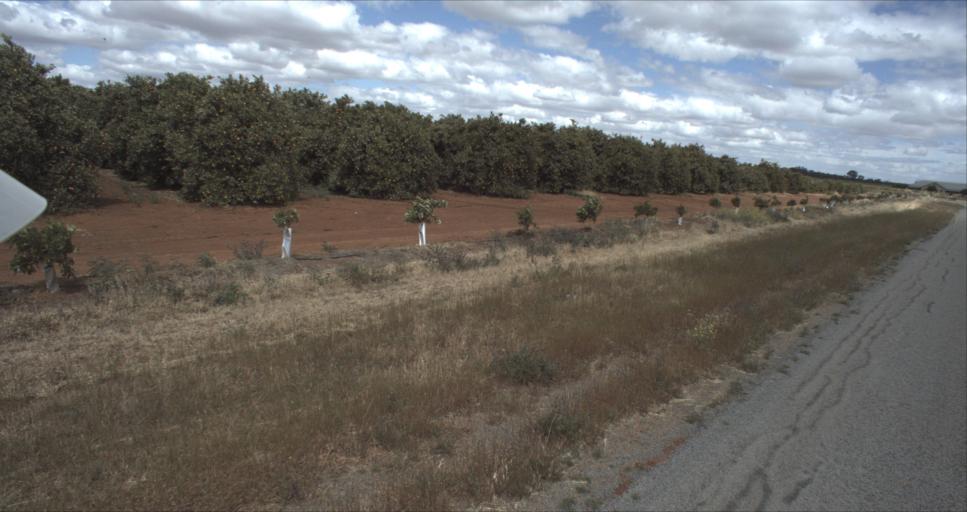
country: AU
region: New South Wales
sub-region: Leeton
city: Leeton
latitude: -34.5879
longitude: 146.3910
